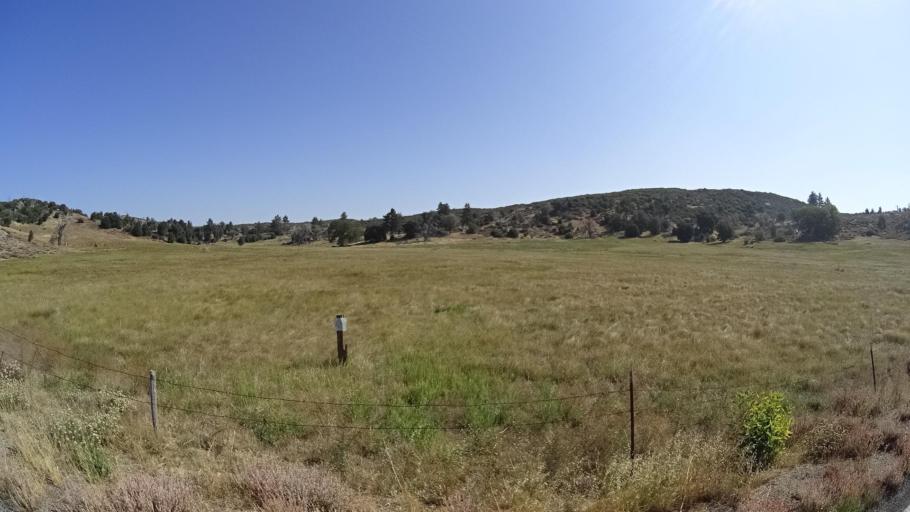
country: US
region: California
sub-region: San Diego County
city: Julian
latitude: 33.0091
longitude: -116.5587
